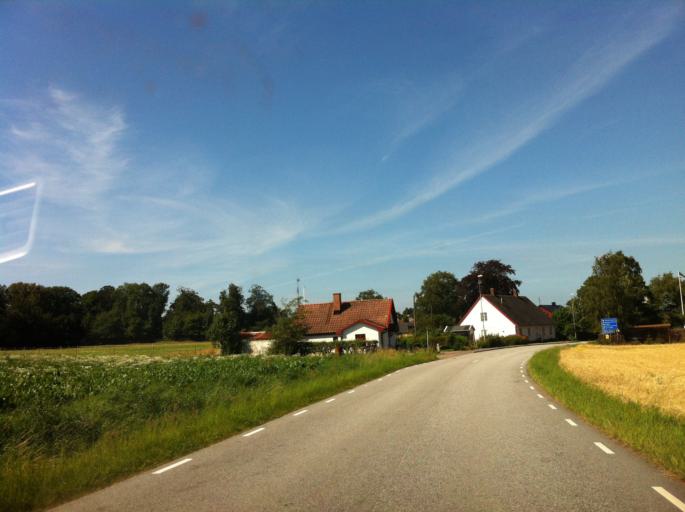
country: SE
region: Skane
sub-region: Landskrona
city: Asmundtorp
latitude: 55.9301
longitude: 12.8869
